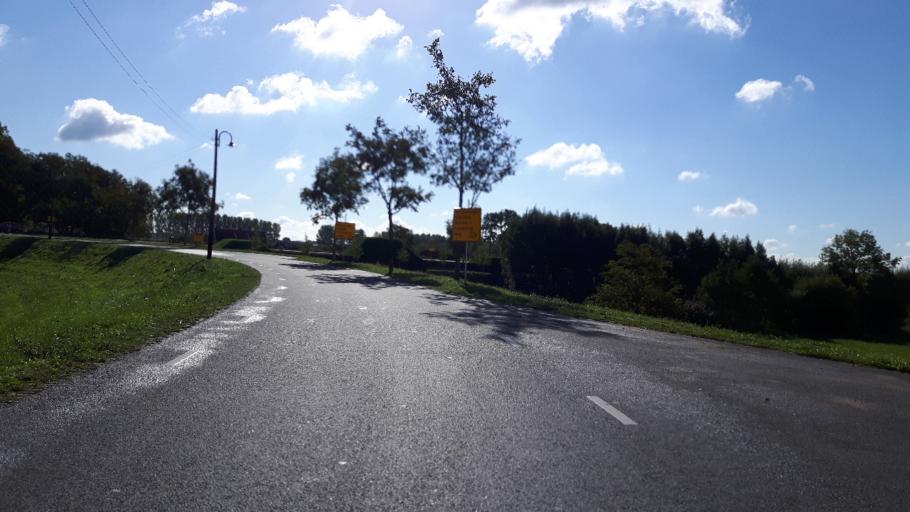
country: NL
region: Gelderland
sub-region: Gemeente Culemborg
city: Culemborg
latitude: 51.9612
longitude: 5.1725
